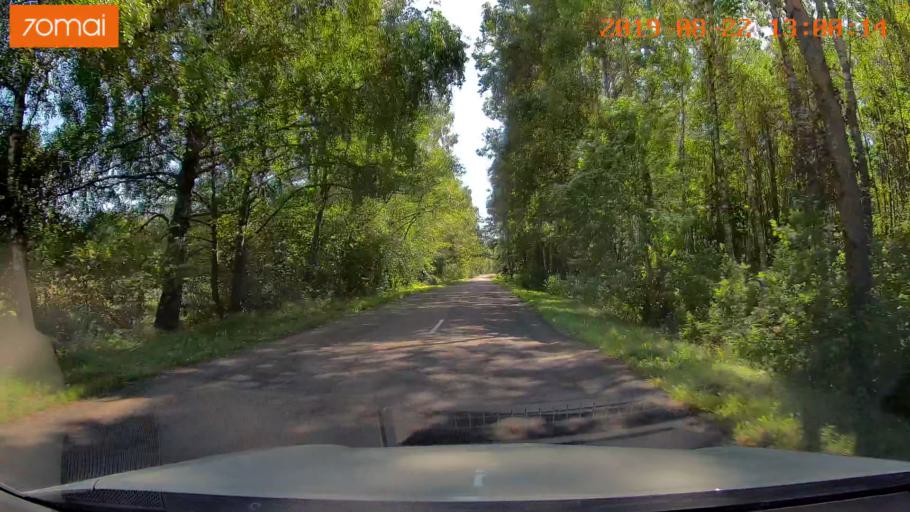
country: BY
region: Minsk
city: Prawdzinski
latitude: 53.4173
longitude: 27.8063
